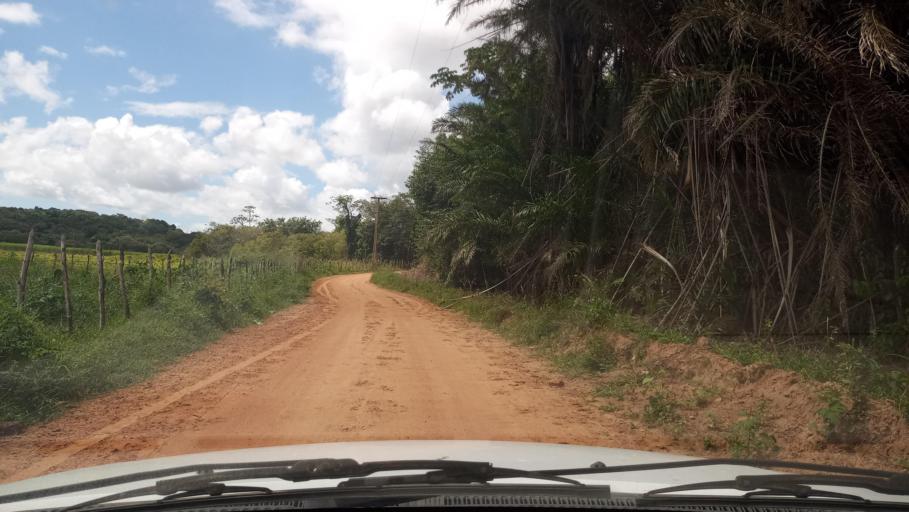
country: BR
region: Rio Grande do Norte
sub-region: Goianinha
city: Goianinha
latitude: -6.2604
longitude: -35.2481
